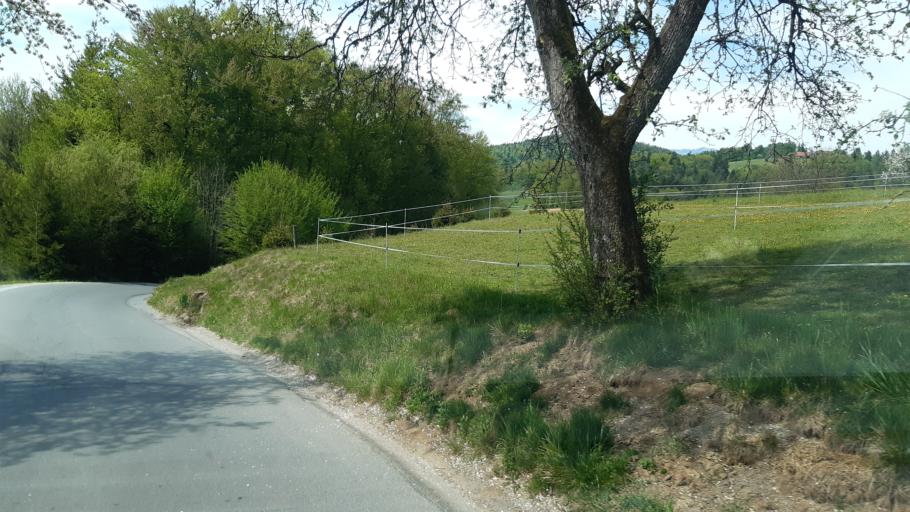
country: SI
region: Lukovica
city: Lukovica pri Domzalah
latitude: 46.1750
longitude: 14.6673
